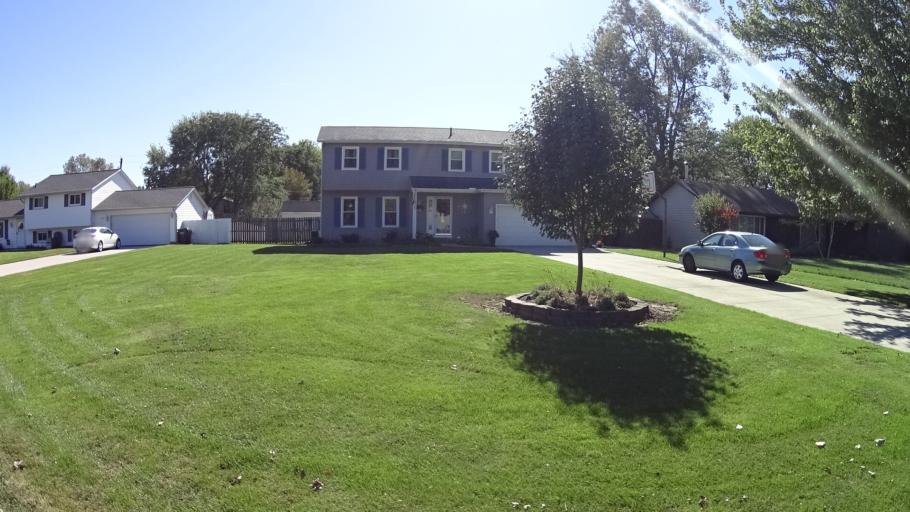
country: US
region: Ohio
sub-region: Lorain County
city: Amherst
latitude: 41.4072
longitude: -82.1864
